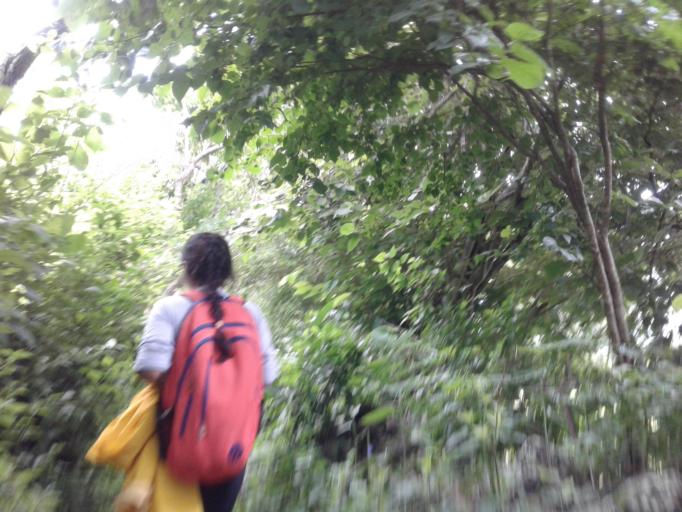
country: NI
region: Leon
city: Santa Rosa del Penon
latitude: 12.9101
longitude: -86.2244
